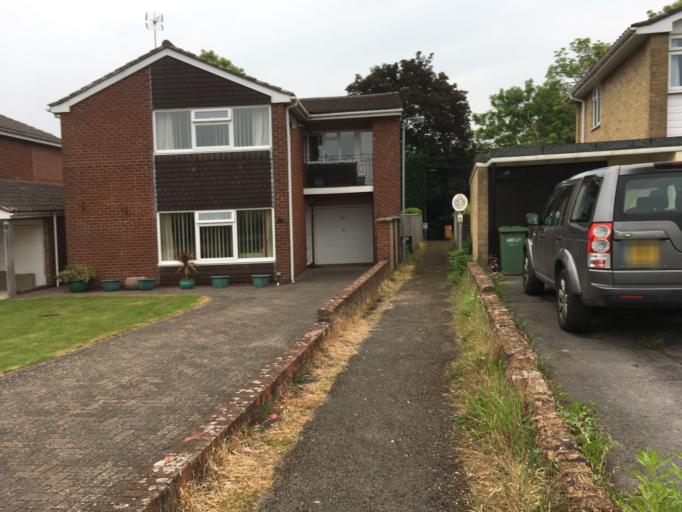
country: GB
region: England
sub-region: South Gloucestershire
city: Thornbury
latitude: 51.6144
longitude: -2.5220
